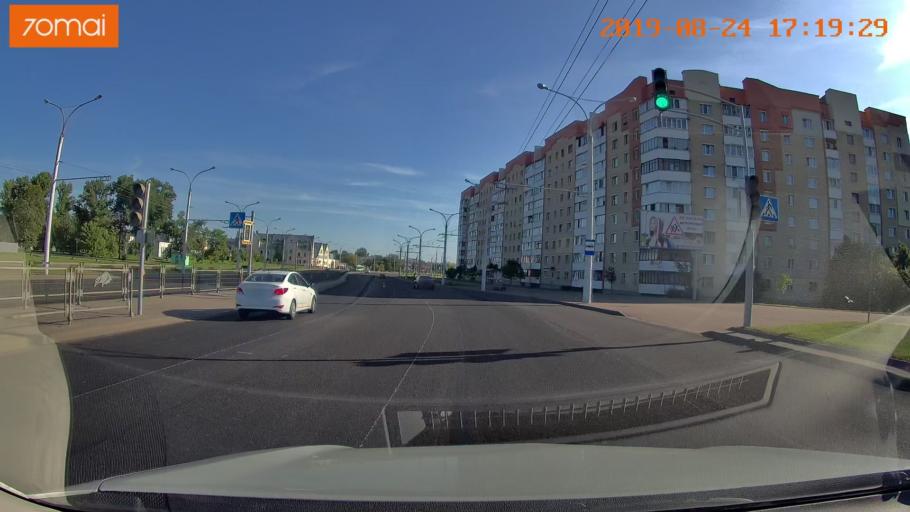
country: BY
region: Minsk
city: Vyaliki Trastsyanets
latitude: 53.8613
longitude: 27.6409
